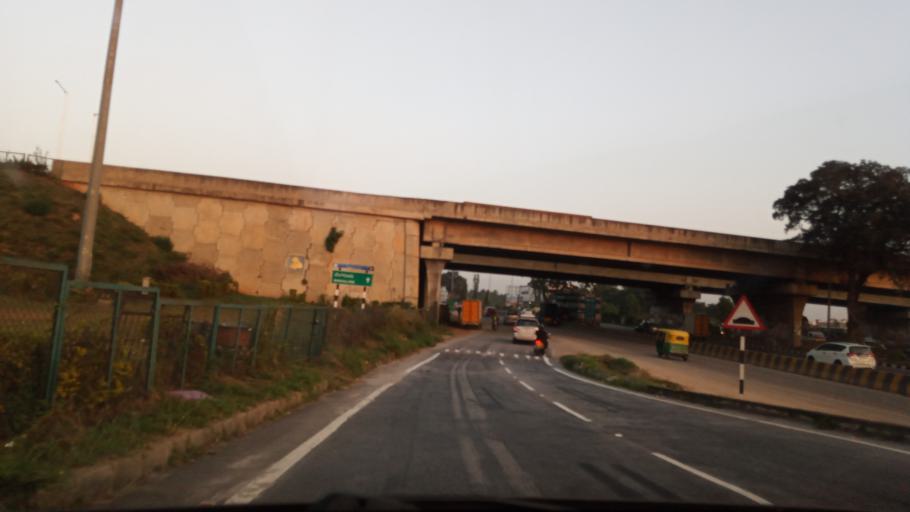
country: IN
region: Karnataka
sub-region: Bangalore Rural
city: Nelamangala
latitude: 13.0564
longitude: 77.4765
